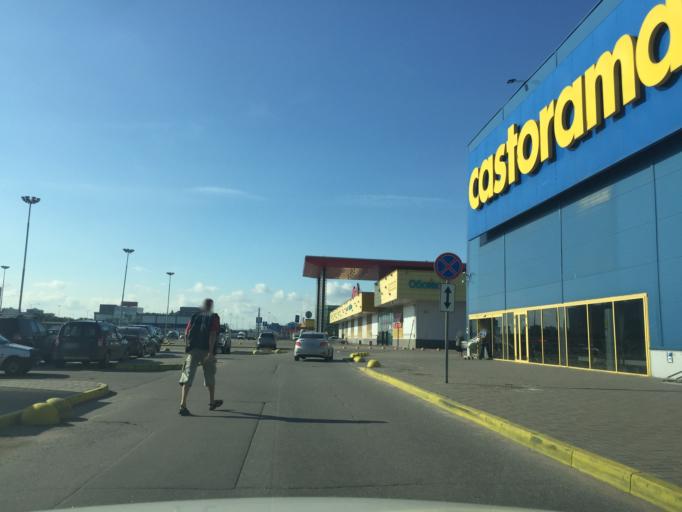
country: RU
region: St.-Petersburg
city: Kupchino
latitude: 59.8288
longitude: 30.3174
